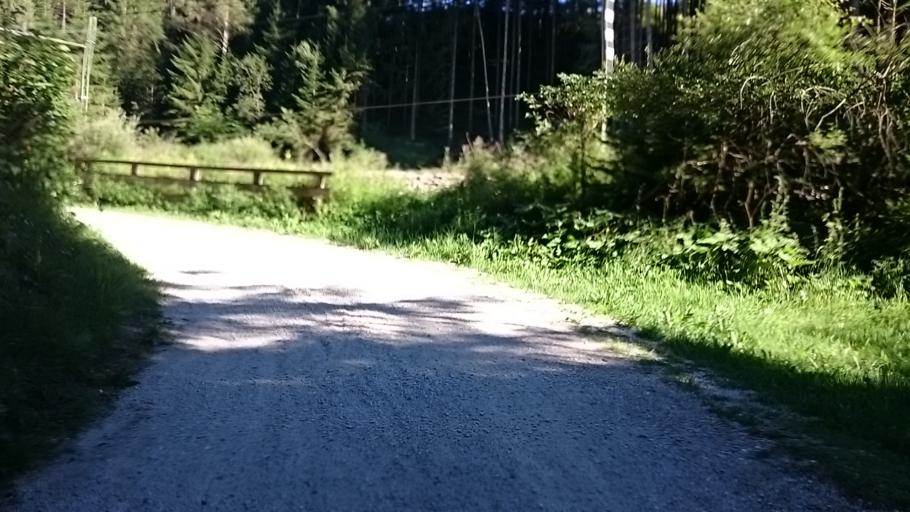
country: IT
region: Trentino-Alto Adige
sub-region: Bolzano
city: Monguelfo
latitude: 46.7592
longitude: 12.0885
